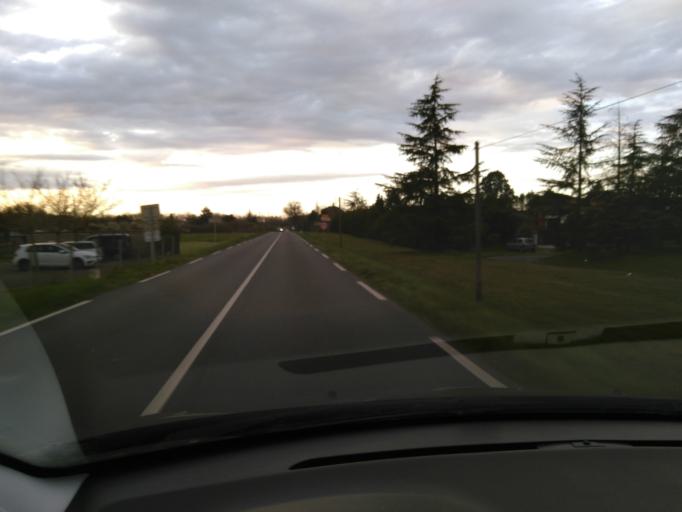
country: FR
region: Midi-Pyrenees
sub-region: Departement de la Haute-Garonne
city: Pibrac
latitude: 43.6112
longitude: 1.2633
